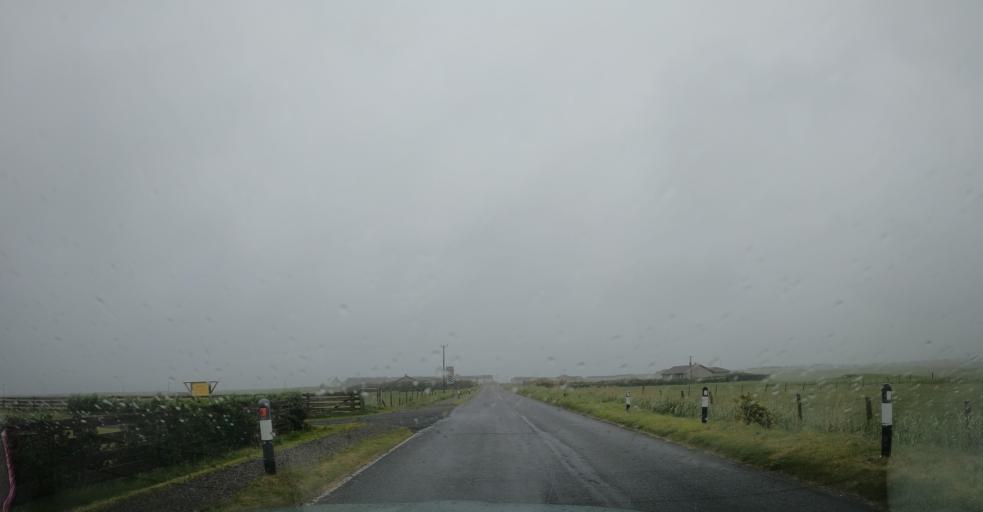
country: GB
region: Scotland
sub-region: Eilean Siar
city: Benbecula
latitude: 57.4682
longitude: -7.3937
